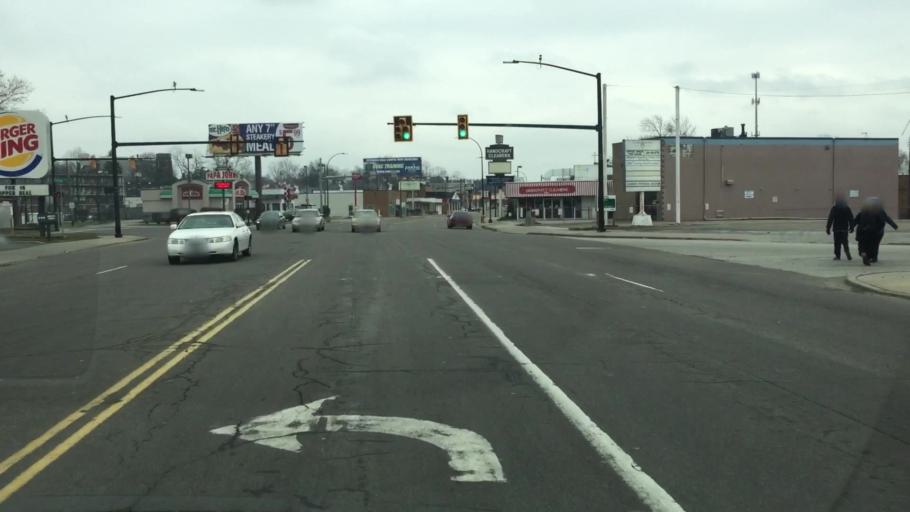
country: US
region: Ohio
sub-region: Summit County
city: Akron
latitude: 41.0769
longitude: -81.4967
